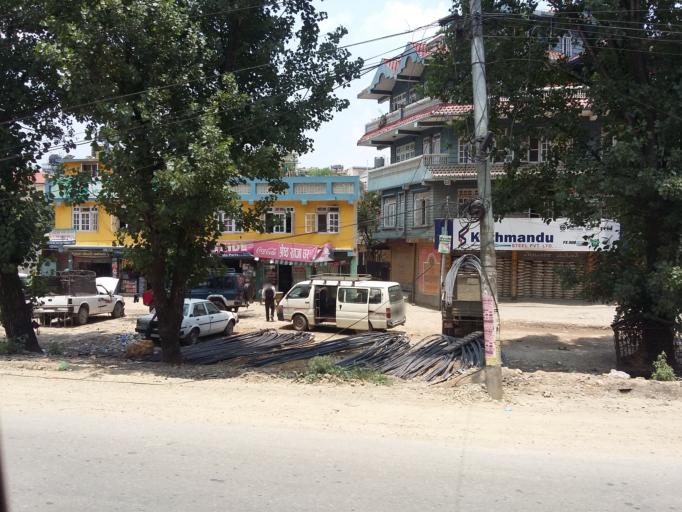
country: NP
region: Central Region
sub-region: Bagmati Zone
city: Kathmandu
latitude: 27.7402
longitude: 85.3285
